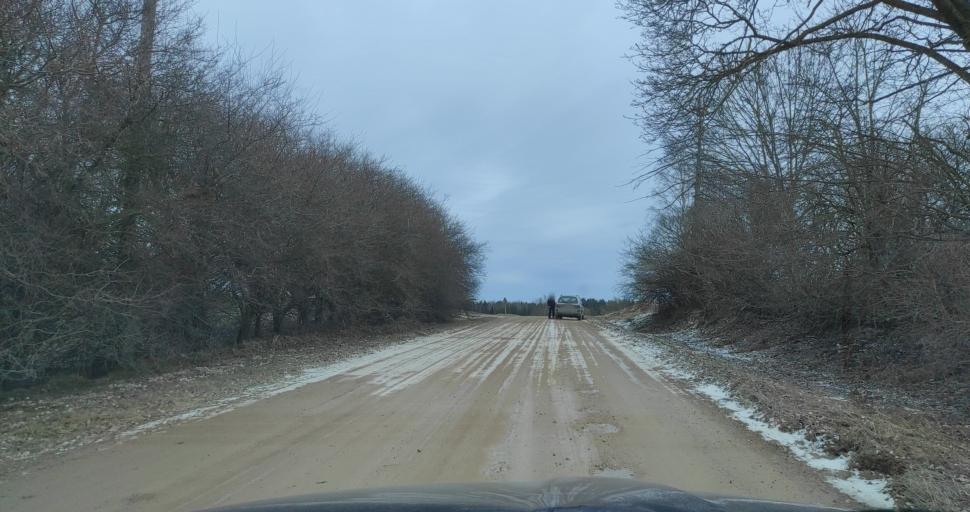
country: LV
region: Tukuma Rajons
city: Tukums
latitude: 57.0651
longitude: 23.0443
